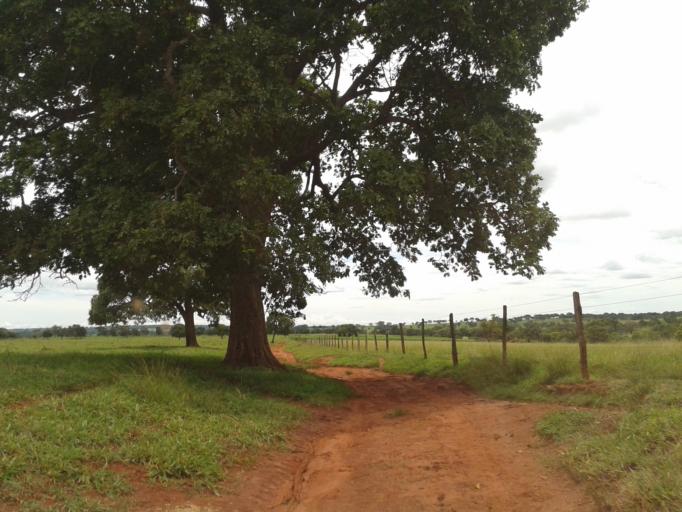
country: BR
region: Minas Gerais
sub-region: Santa Vitoria
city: Santa Vitoria
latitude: -18.7869
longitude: -49.8523
